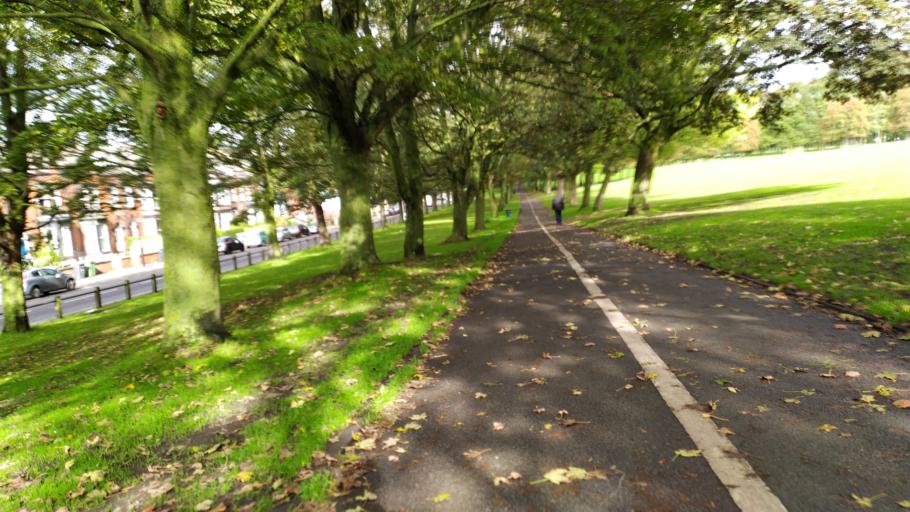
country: GB
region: England
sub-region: City and Borough of Leeds
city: Leeds
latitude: 53.8109
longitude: -1.5647
